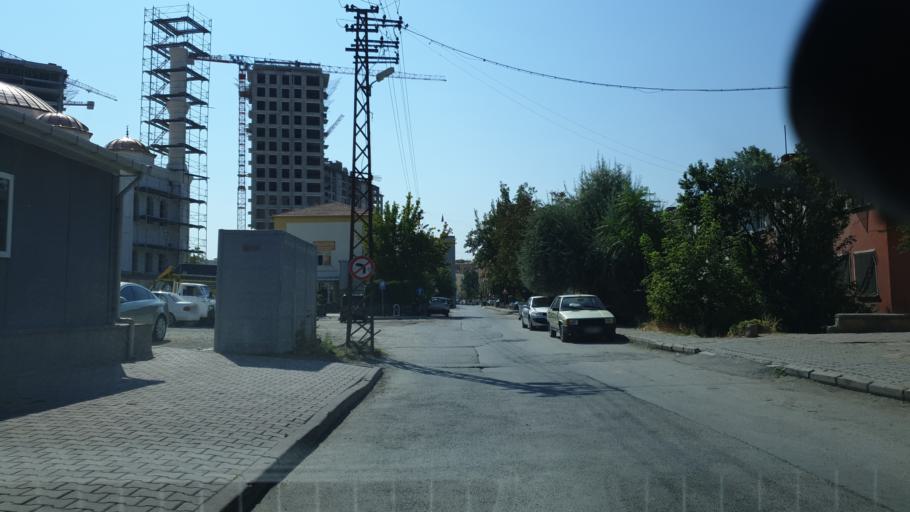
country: TR
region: Kayseri
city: Kayseri
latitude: 38.7297
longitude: 35.4888
